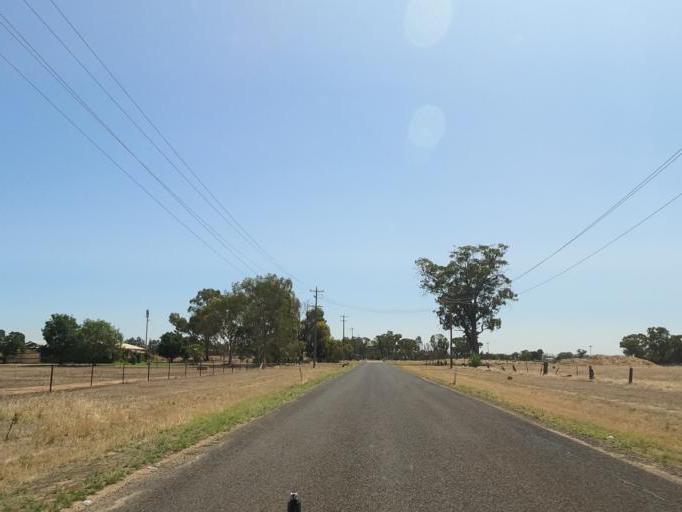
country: AU
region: New South Wales
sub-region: Corowa Shire
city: Mulwala
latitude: -35.9801
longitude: 146.0040
